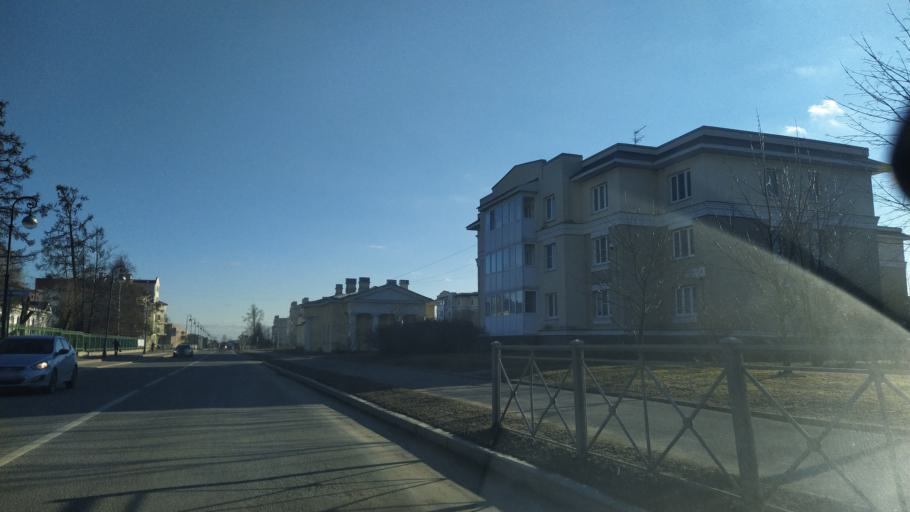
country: RU
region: St.-Petersburg
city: Pushkin
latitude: 59.7051
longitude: 30.3917
